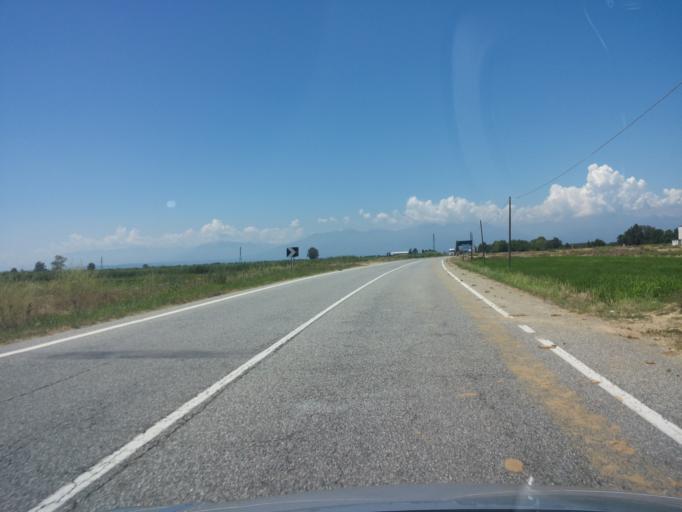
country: IT
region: Piedmont
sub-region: Provincia di Vercelli
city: Formigliana
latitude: 45.4165
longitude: 8.3134
